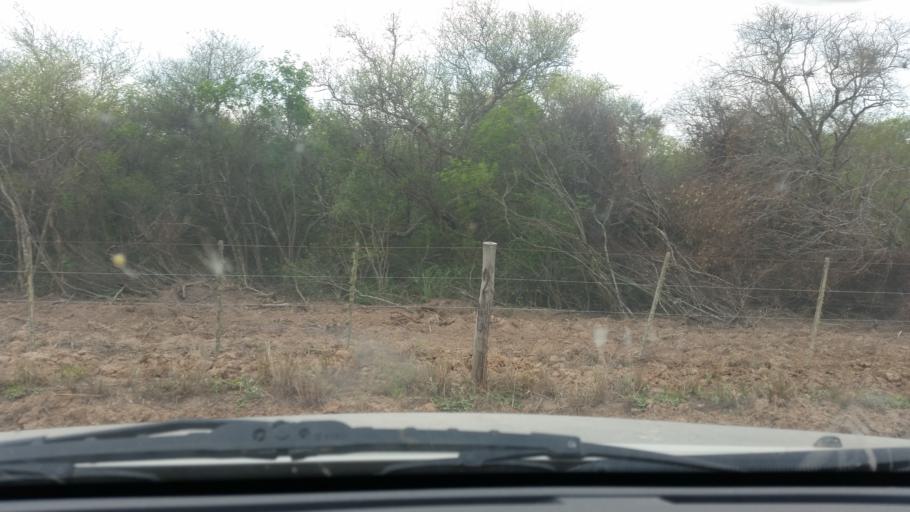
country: PY
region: Boqueron
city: Colonia Menno
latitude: -22.3559
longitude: -59.3395
